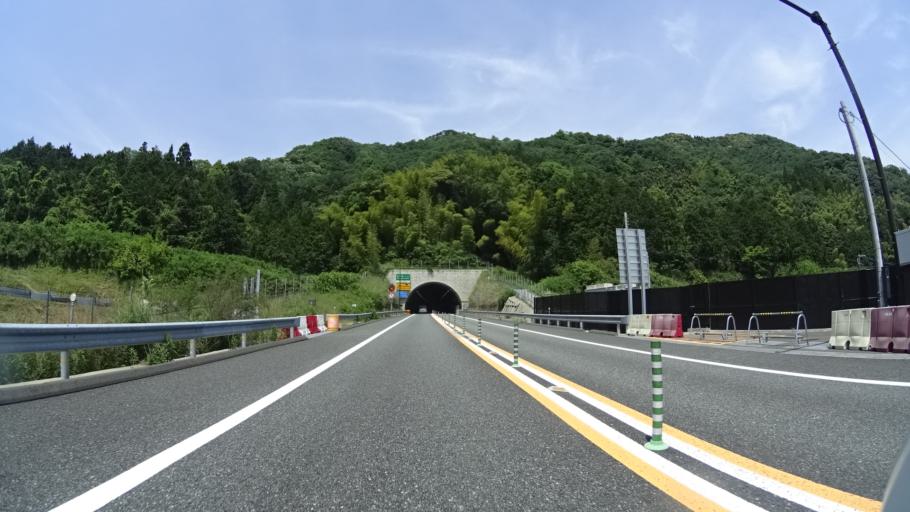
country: JP
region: Kyoto
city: Miyazu
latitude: 35.5527
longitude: 135.1342
